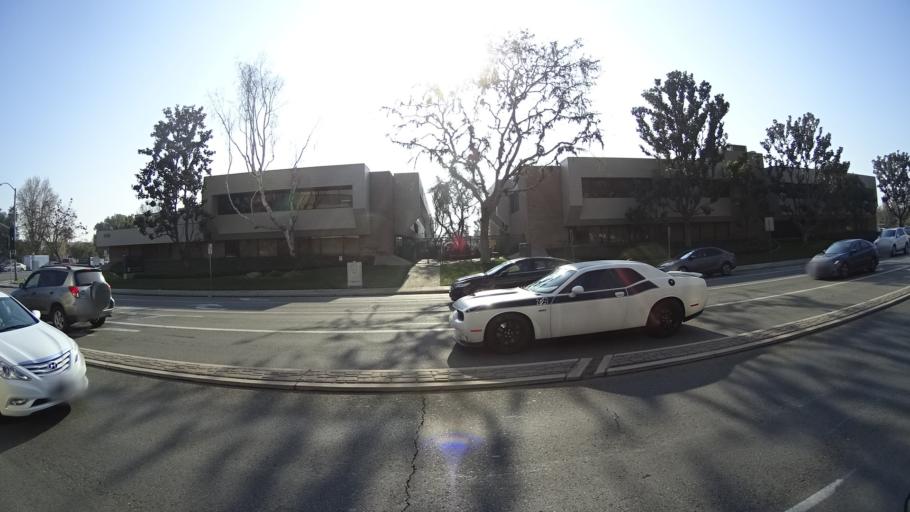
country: US
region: California
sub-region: Kern County
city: Bakersfield
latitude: 35.3614
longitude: -119.0604
